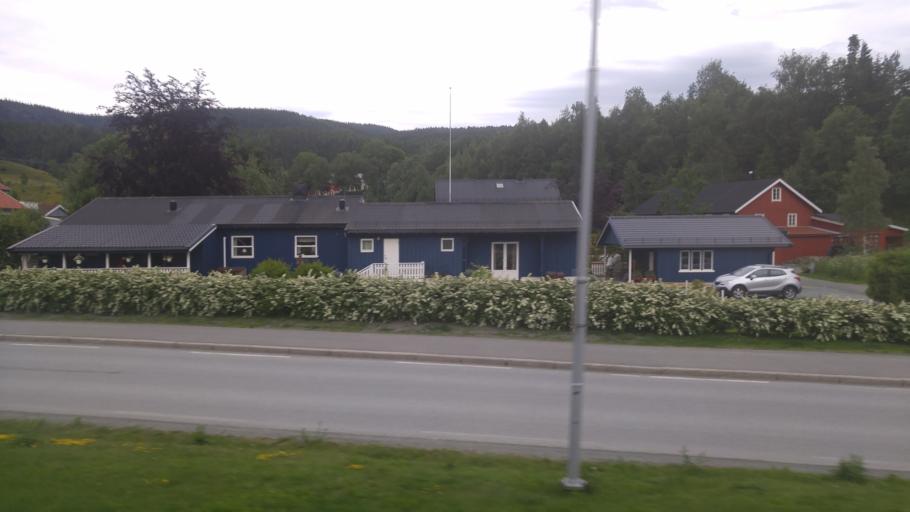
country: NO
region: Nord-Trondelag
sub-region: Stjordal
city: Stjordalshalsen
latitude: 63.4610
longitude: 11.1016
